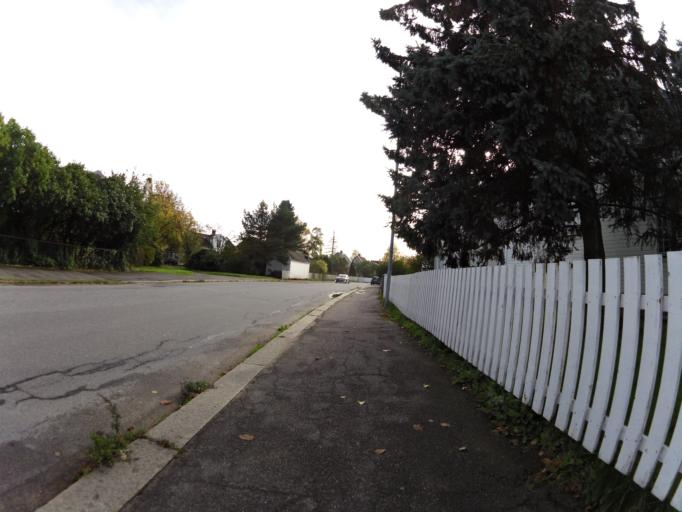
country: NO
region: Ostfold
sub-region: Fredrikstad
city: Fredrikstad
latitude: 59.2186
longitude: 10.9306
